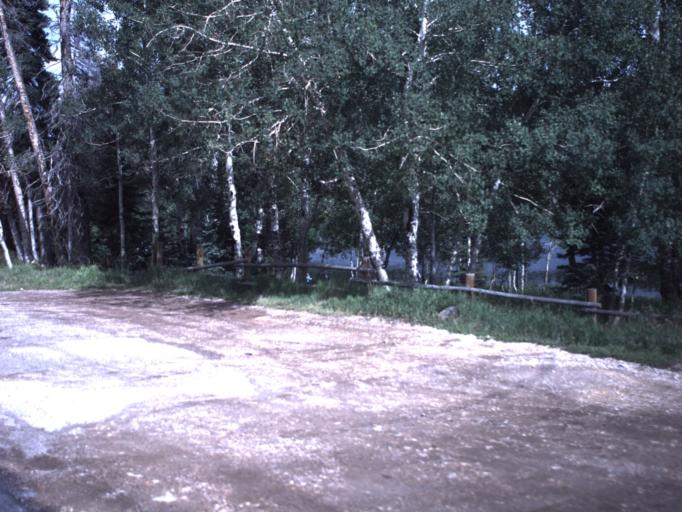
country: US
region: Utah
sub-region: Iron County
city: Parowan
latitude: 37.5151
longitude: -112.6956
